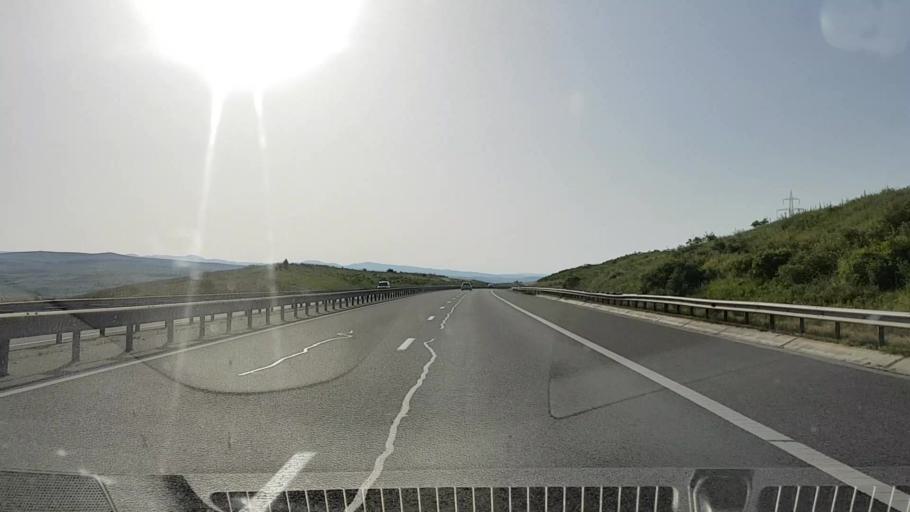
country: RO
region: Cluj
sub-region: Comuna Petrestii De Jos
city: Petrestii de Jos
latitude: 46.6011
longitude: 23.6221
